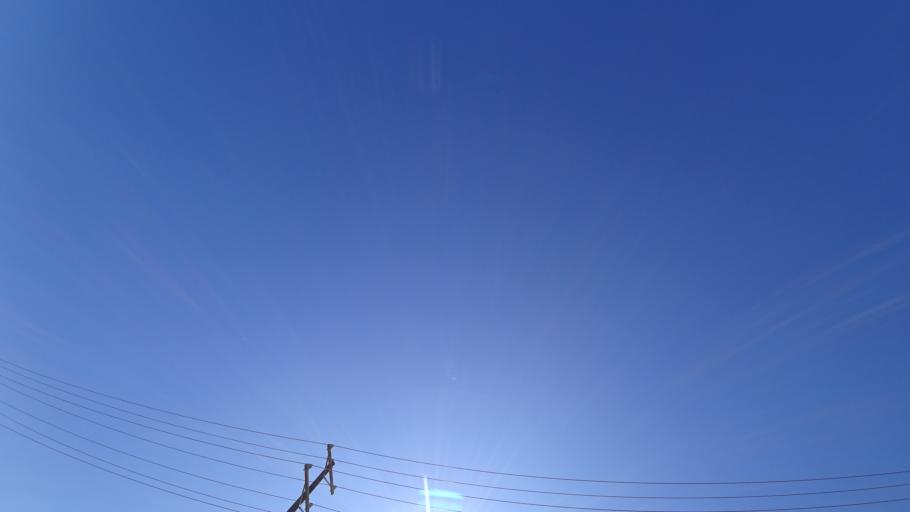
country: US
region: Texas
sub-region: Denton County
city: Lewisville
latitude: 33.0467
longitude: -96.9323
